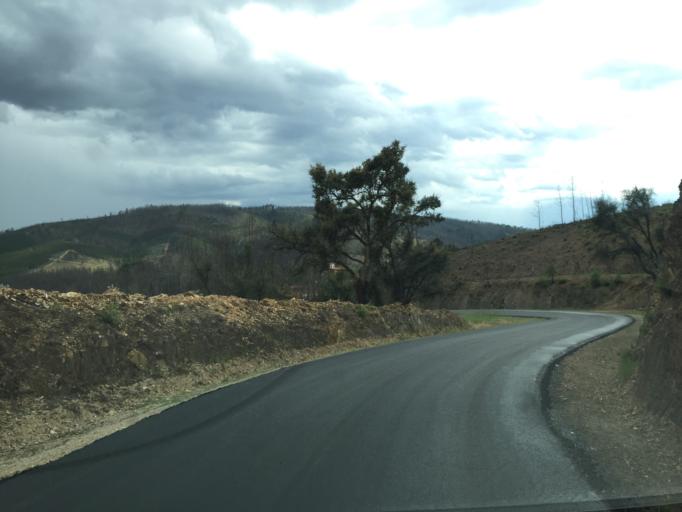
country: PT
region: Coimbra
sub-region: Pampilhosa da Serra
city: Pampilhosa da Serra
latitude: 40.0562
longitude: -8.0170
